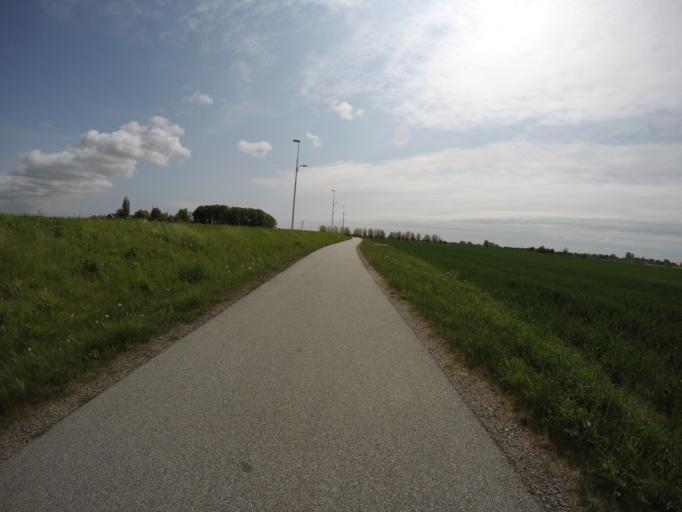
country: SE
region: Skane
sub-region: Malmo
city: Bunkeflostrand
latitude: 55.5432
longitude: 12.9805
